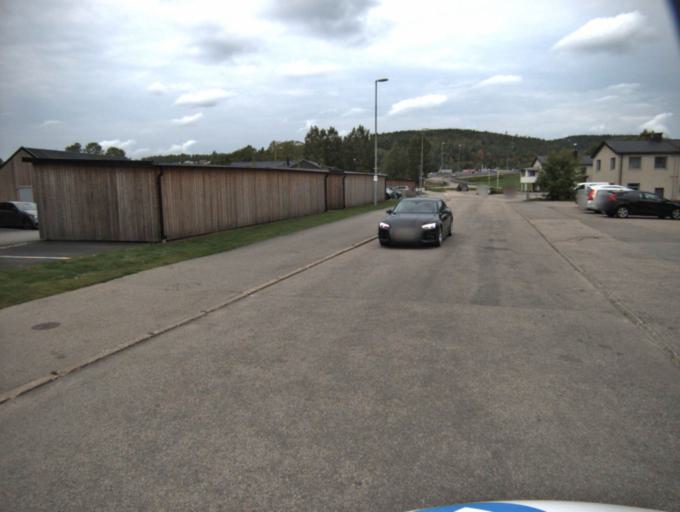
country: SE
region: Vaestra Goetaland
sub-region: Ulricehamns Kommun
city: Ulricehamn
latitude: 57.8018
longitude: 13.4117
